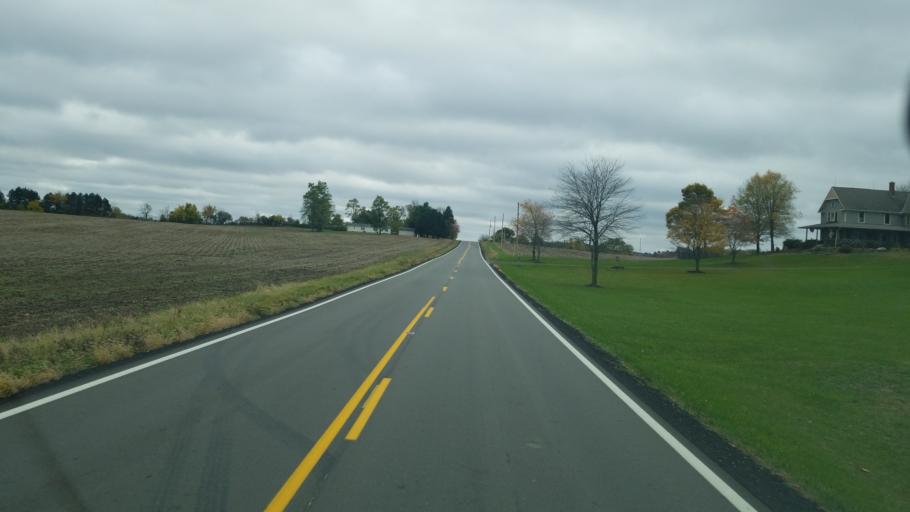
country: US
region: Ohio
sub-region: Huron County
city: Plymouth
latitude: 40.9772
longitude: -82.7111
